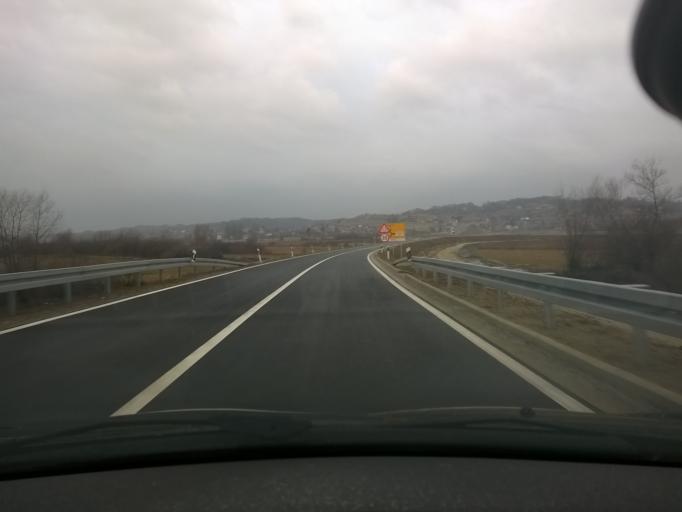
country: HR
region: Krapinsko-Zagorska
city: Bedekovcina
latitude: 46.0349
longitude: 15.9894
